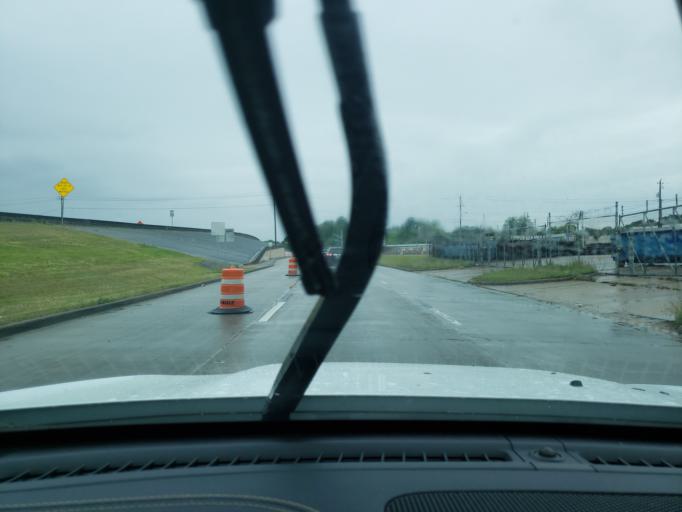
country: US
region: Texas
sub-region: Harris County
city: Baytown
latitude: 29.7560
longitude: -94.9406
